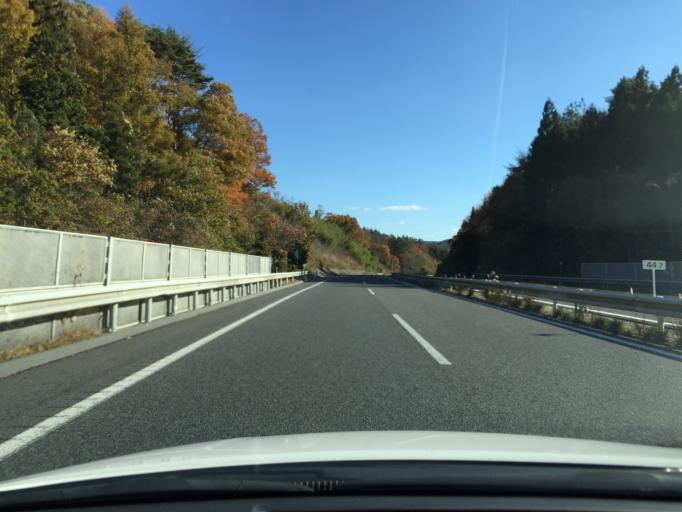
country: JP
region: Fukushima
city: Funehikimachi-funehiki
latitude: 37.3709
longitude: 140.6037
